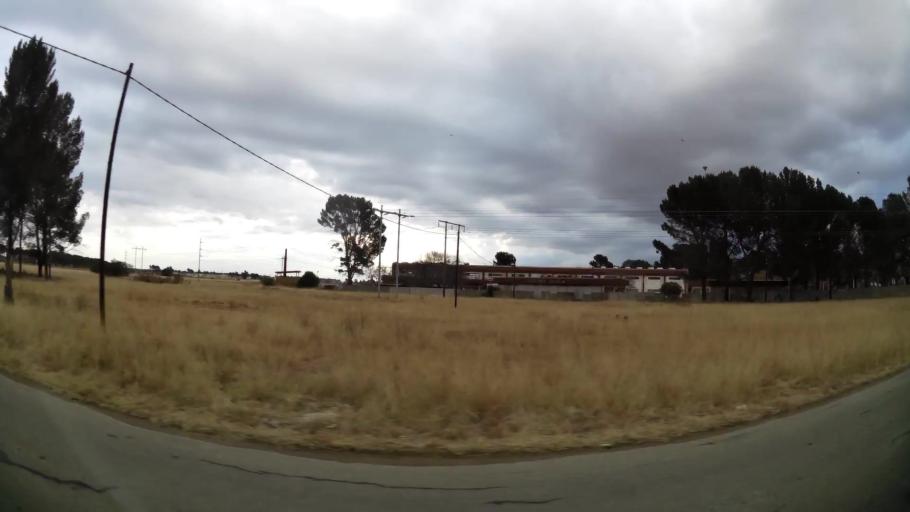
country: ZA
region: Orange Free State
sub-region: Lejweleputswa District Municipality
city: Welkom
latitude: -27.9628
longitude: 26.7154
